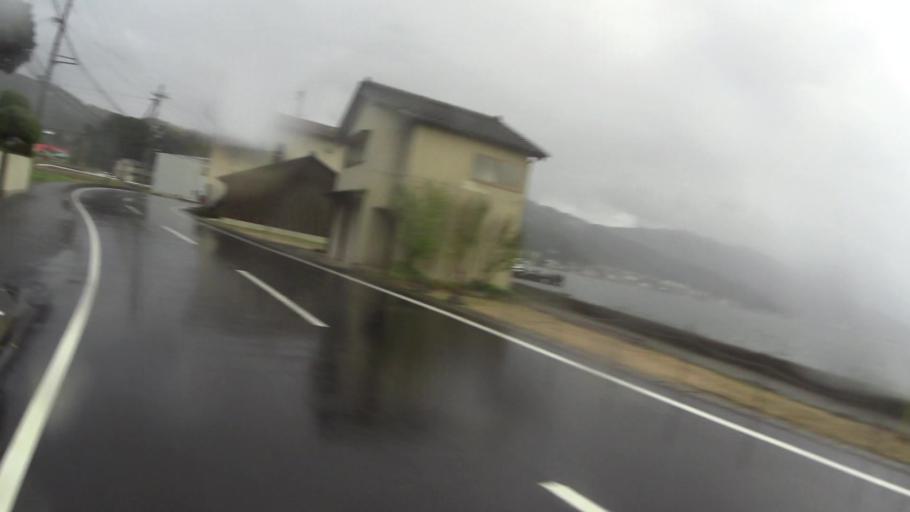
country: JP
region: Kyoto
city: Miyazu
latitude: 35.5539
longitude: 135.2082
